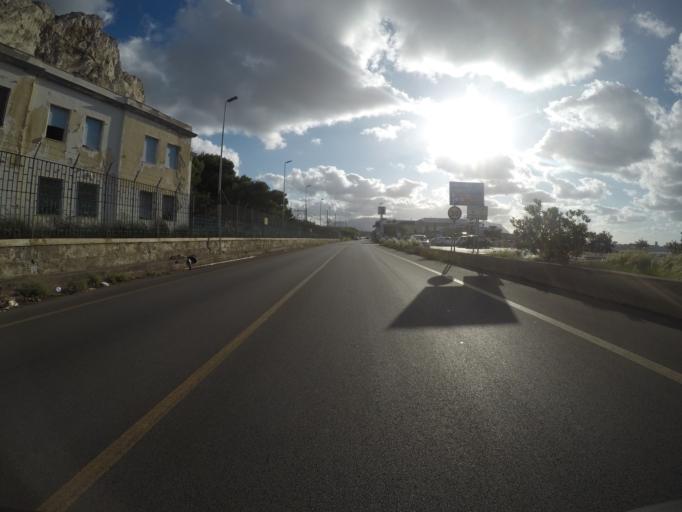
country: IT
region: Sicily
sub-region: Palermo
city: Isola delle Femmine
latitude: 38.2002
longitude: 13.2573
